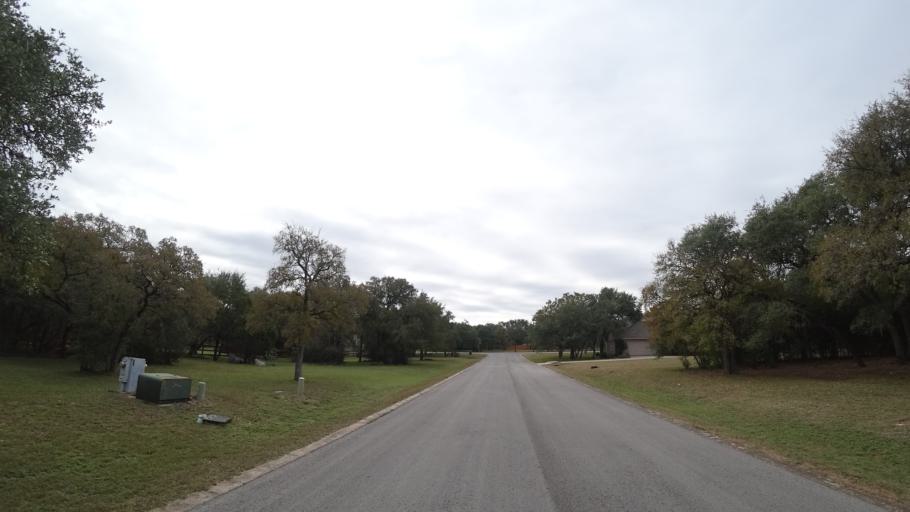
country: US
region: Texas
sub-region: Travis County
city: Shady Hollow
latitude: 30.1412
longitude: -97.8813
